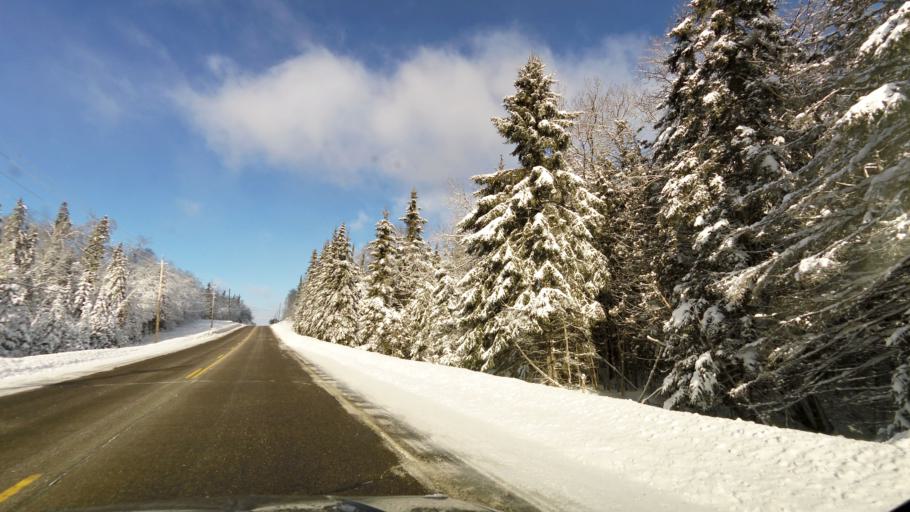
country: CA
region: Ontario
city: Bancroft
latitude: 44.9950
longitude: -78.2995
